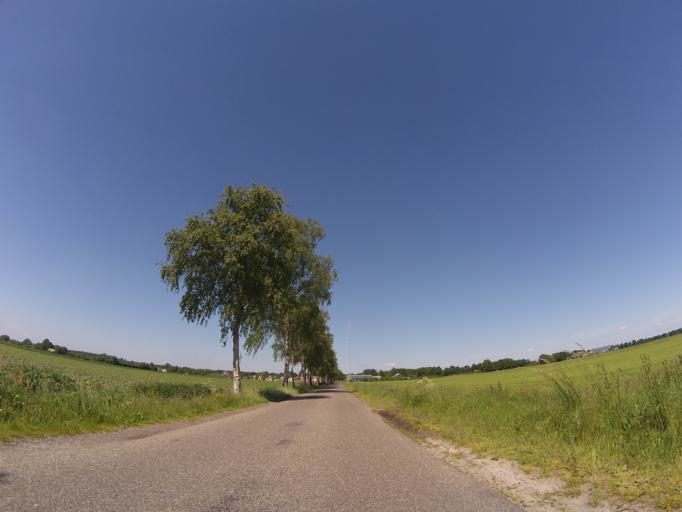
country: NL
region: Drenthe
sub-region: Gemeente Hoogeveen
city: Hoogeveen
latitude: 52.7636
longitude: 6.6159
